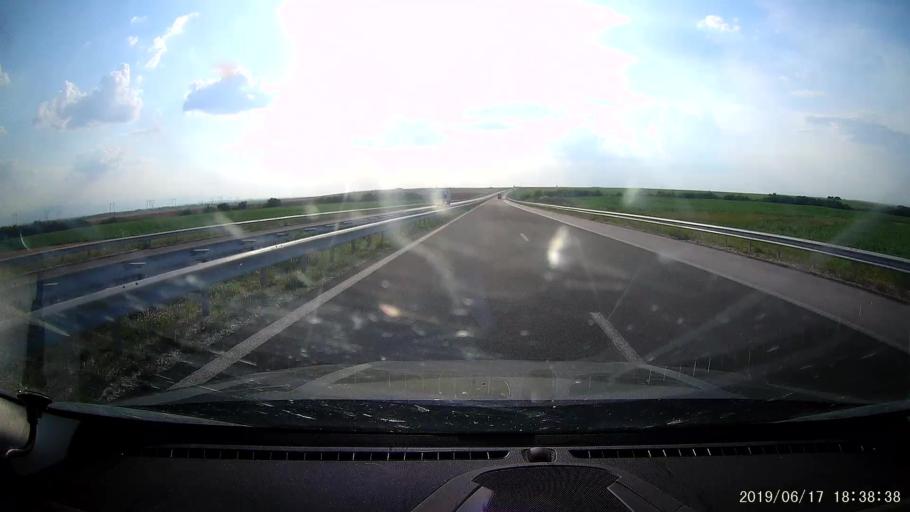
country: BG
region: Stara Zagora
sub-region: Obshtina Chirpan
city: Chirpan
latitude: 42.1381
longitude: 25.3314
